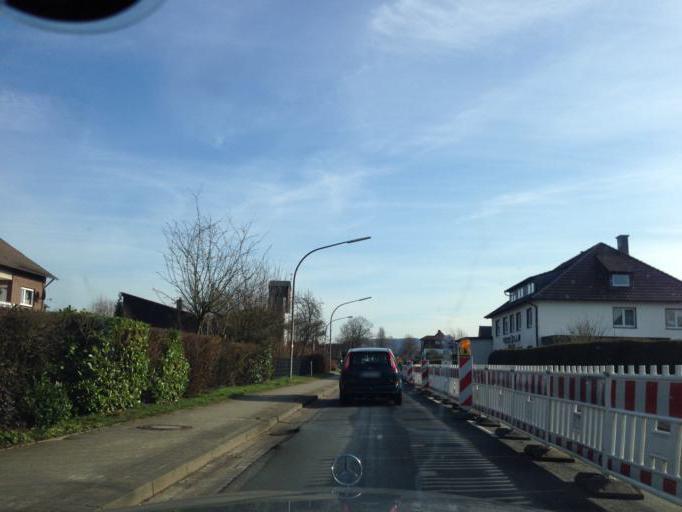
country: DE
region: Lower Saxony
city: Hasbergen
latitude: 52.2057
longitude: 7.9267
